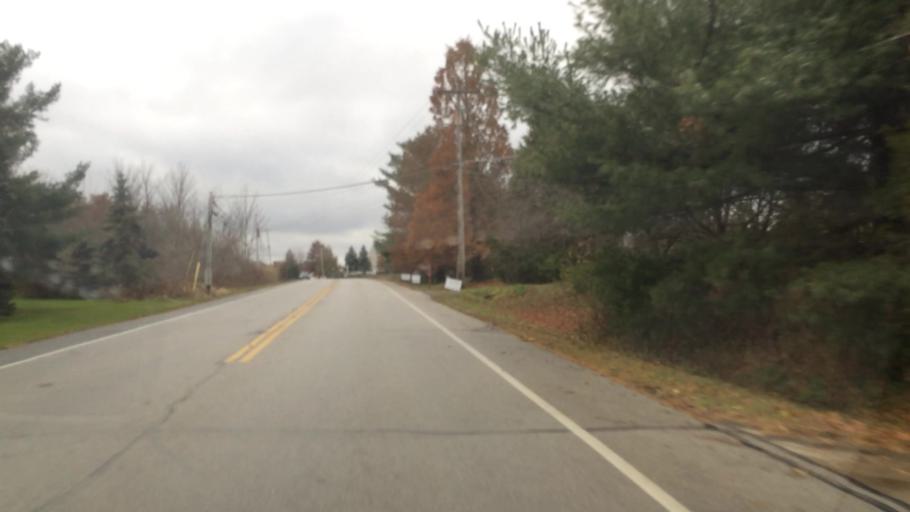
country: US
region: Ohio
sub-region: Summit County
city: Stow
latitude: 41.1937
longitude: -81.4206
